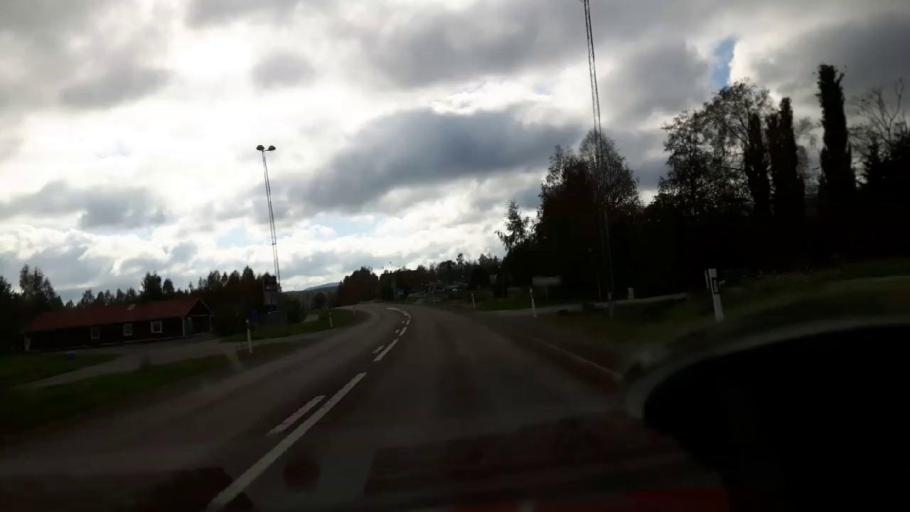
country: SE
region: Gaevleborg
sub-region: Ljusdals Kommun
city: Jaervsoe
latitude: 61.6745
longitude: 16.1449
